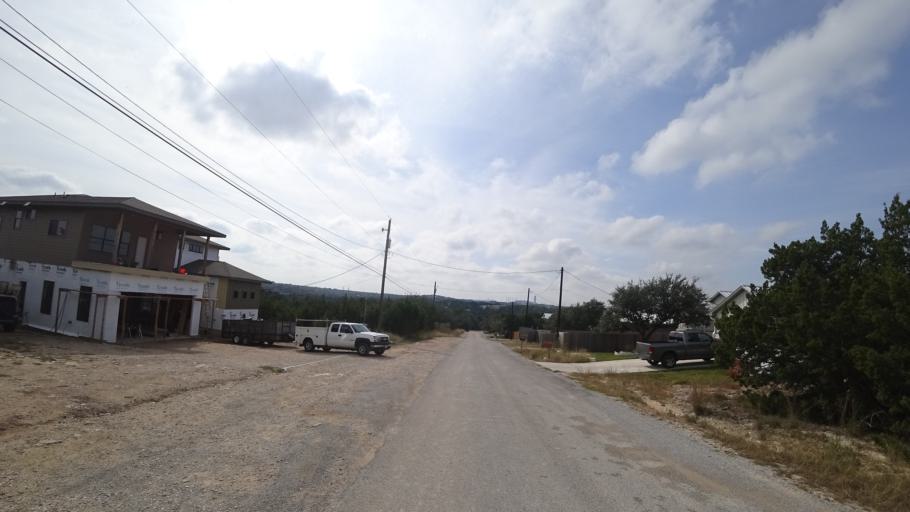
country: US
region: Texas
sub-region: Travis County
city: Hudson Bend
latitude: 30.3871
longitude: -97.9341
